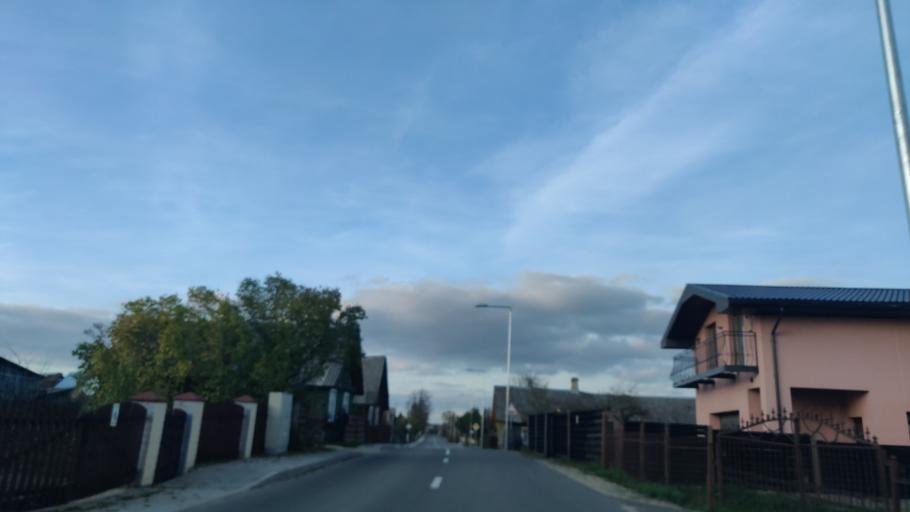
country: LT
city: Lentvaris
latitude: 54.5827
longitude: 25.0514
